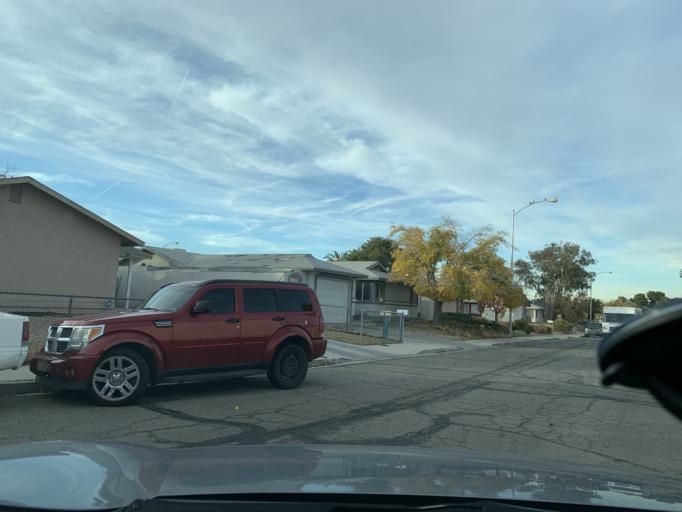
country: US
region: Nevada
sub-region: Clark County
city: Spring Valley
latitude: 36.0980
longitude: -115.2334
